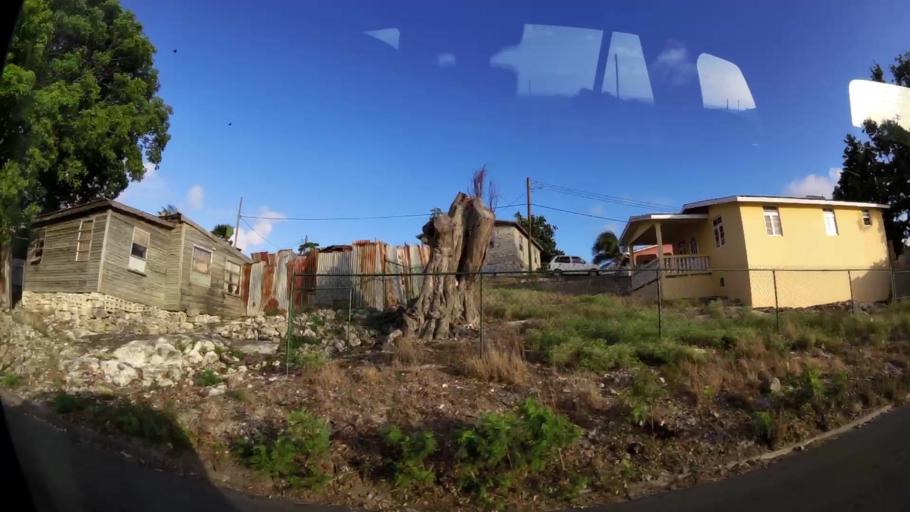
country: BB
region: Christ Church
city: Oistins
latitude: 13.0789
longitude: -59.5063
